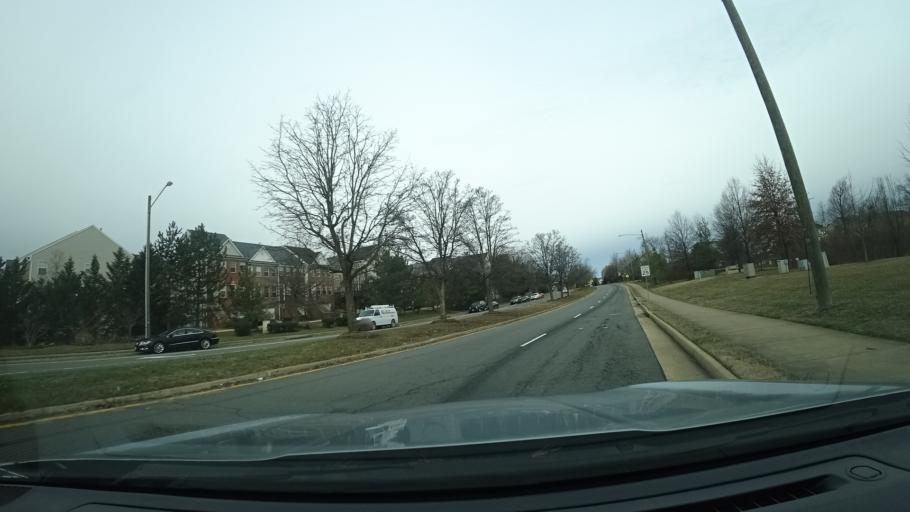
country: US
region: Virginia
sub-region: Fairfax County
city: Floris
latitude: 38.9428
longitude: -77.4054
